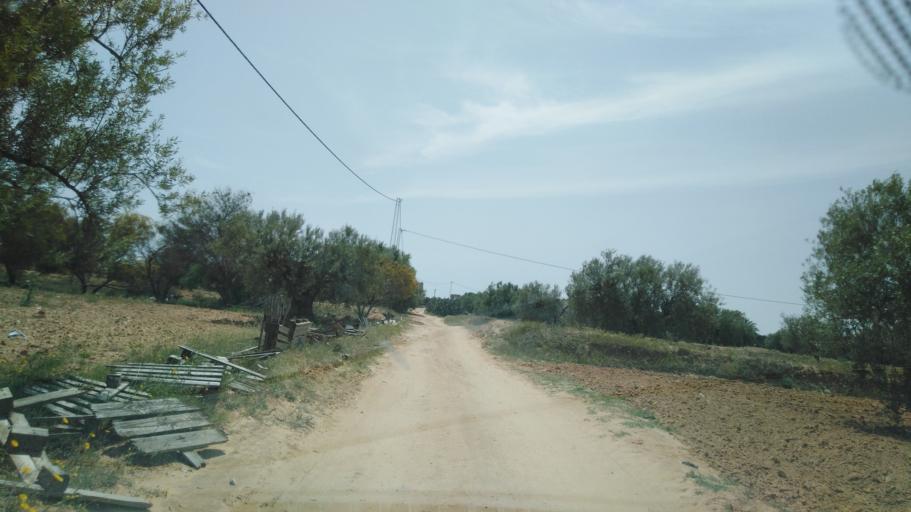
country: TN
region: Safaqis
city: Sfax
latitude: 34.7302
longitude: 10.5556
